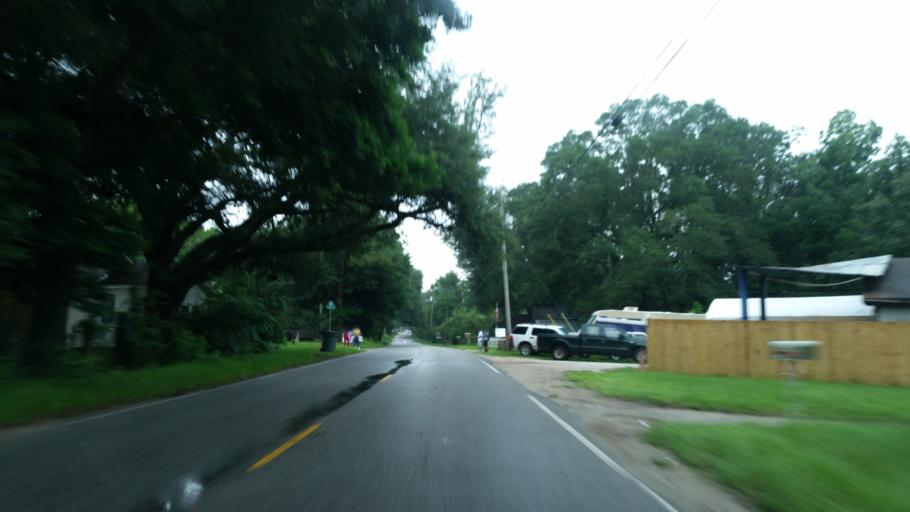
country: US
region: Florida
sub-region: Escambia County
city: West Pensacola
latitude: 30.4274
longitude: -87.2618
